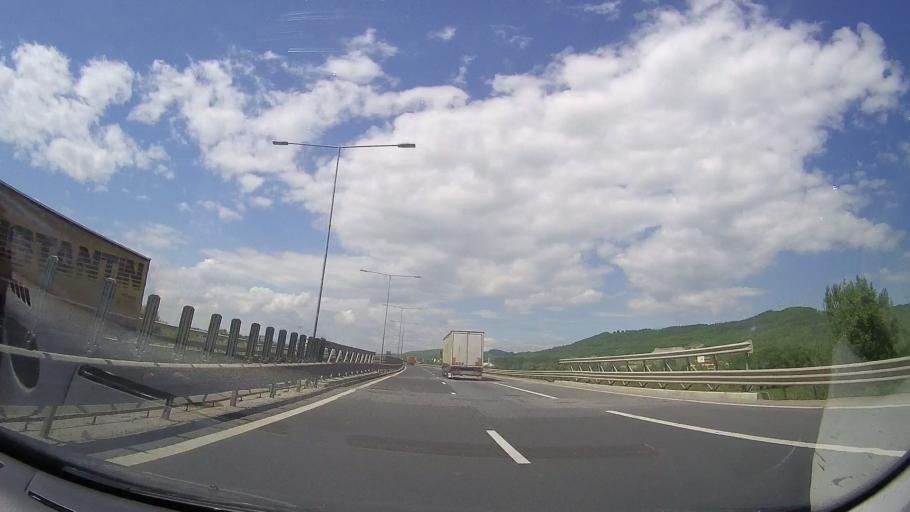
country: RO
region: Sibiu
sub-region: Comuna Selimbar
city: Selimbar
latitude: 45.7931
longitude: 24.1970
